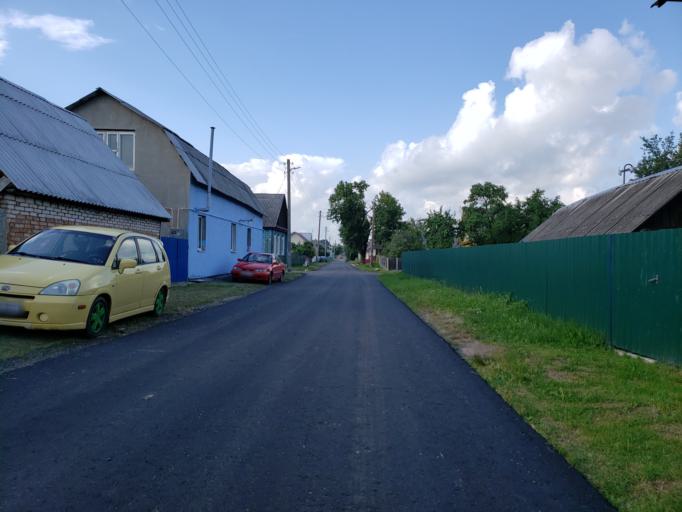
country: BY
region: Minsk
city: Chervyen'
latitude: 53.7075
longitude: 28.4266
